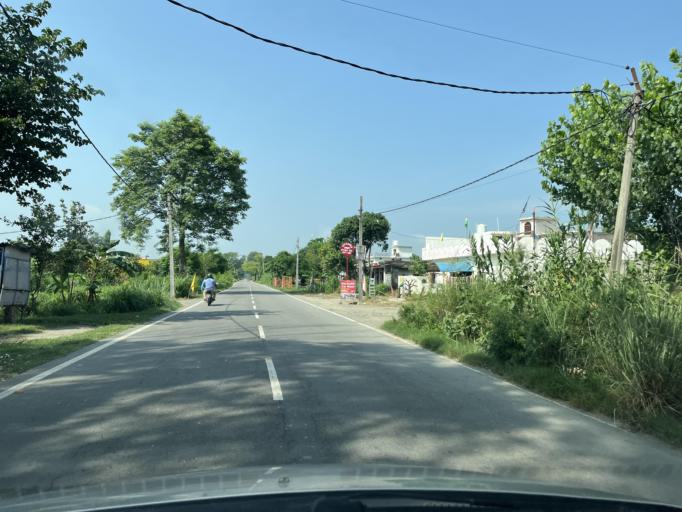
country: IN
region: Uttarakhand
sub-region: Udham Singh Nagar
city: Bazpur
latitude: 29.2024
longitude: 79.2059
